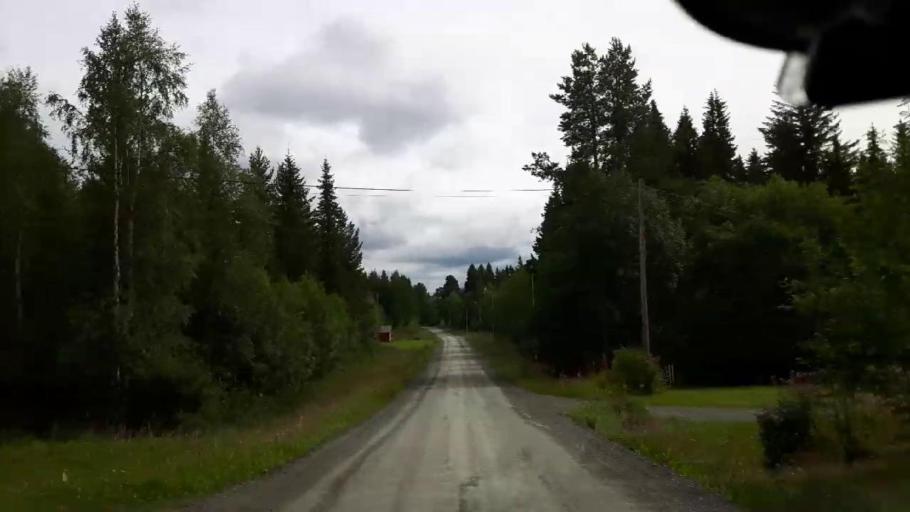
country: SE
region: Jaemtland
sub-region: Krokoms Kommun
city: Valla
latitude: 63.6276
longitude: 14.0251
